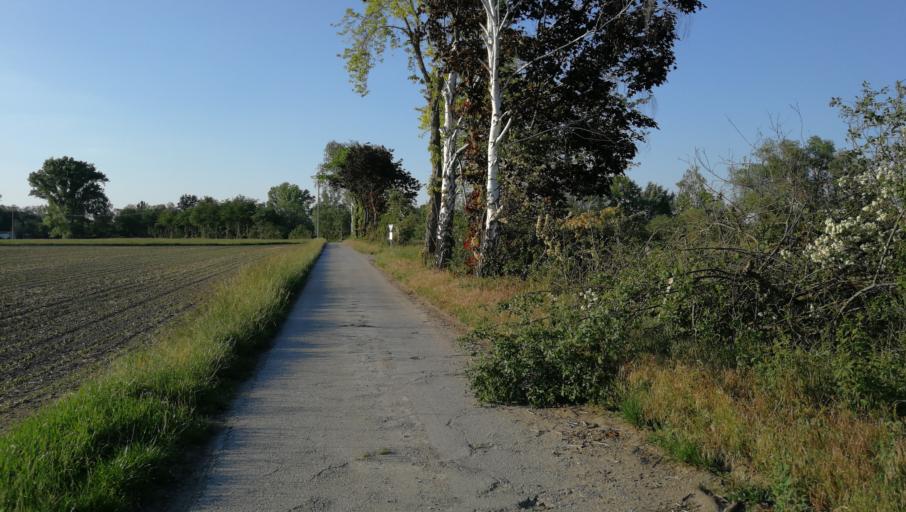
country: DE
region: Baden-Wuerttemberg
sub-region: Karlsruhe Region
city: Altlussheim
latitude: 49.3145
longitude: 8.4886
